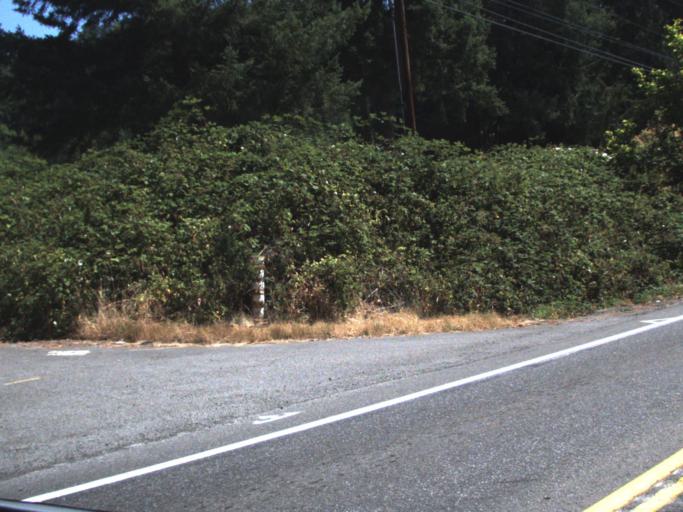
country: US
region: Washington
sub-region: King County
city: Union Hill-Novelty Hill
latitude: 47.6438
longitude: -122.0226
